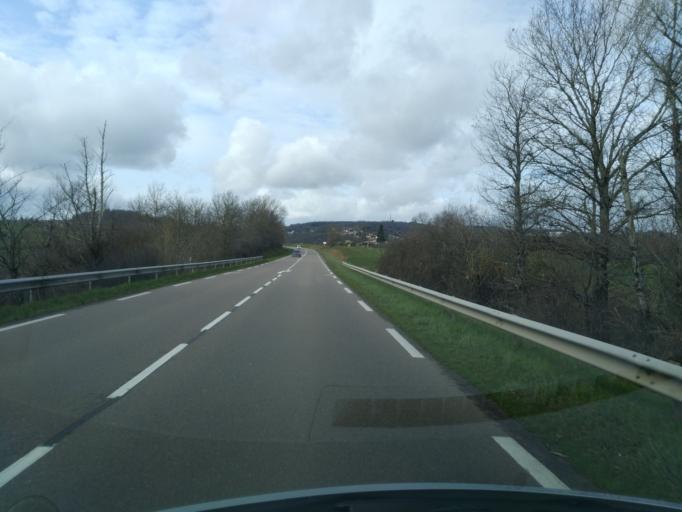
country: FR
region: Bourgogne
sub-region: Departement de Saone-et-Loire
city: Le Creusot
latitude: 46.7795
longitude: 4.4177
